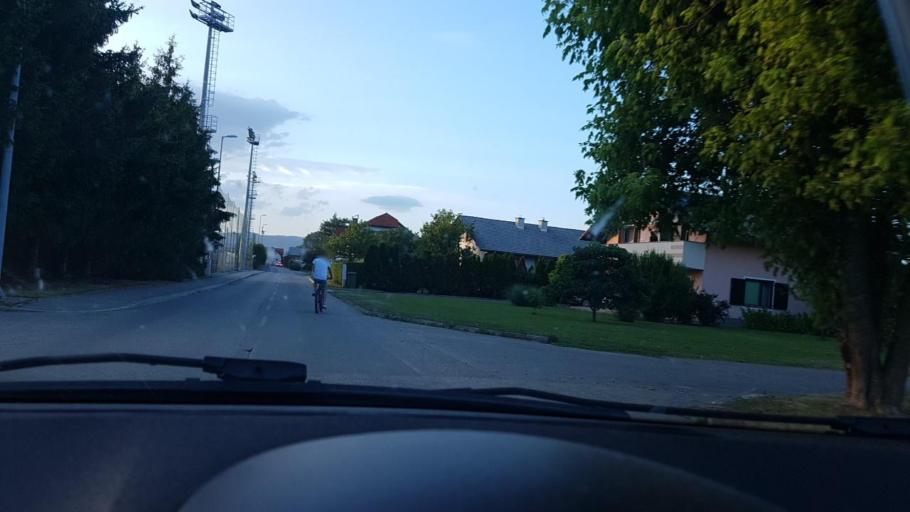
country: SI
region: Brezice
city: Brezice
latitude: 45.9096
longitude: 15.5930
